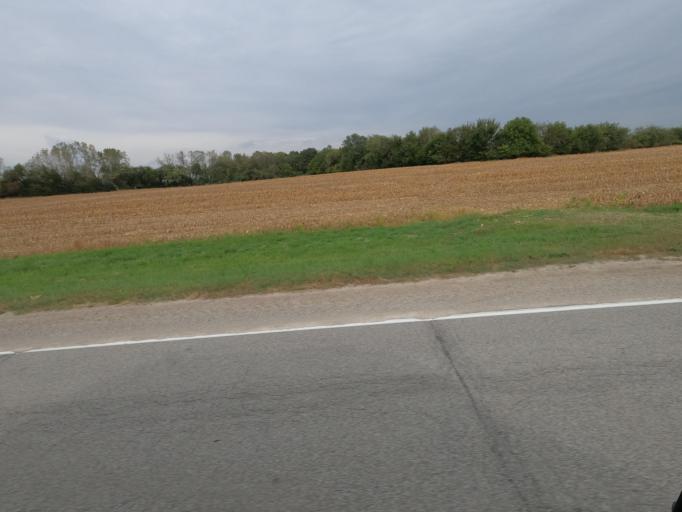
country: US
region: Iowa
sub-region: Van Buren County
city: Keosauqua
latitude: 40.8637
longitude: -92.1371
